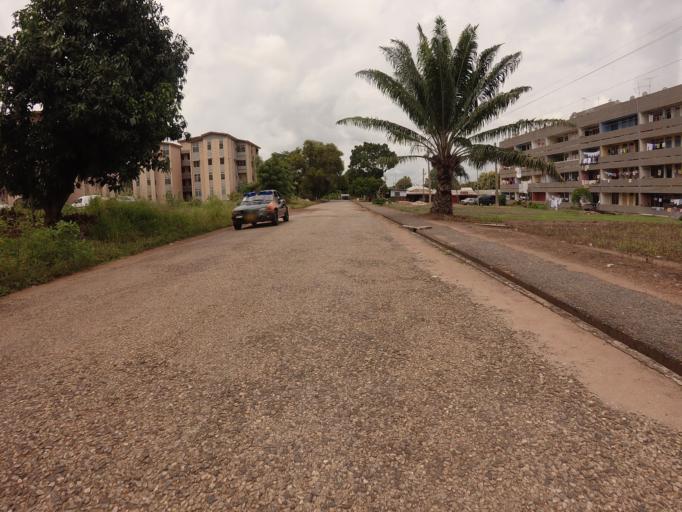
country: GH
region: Volta
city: Ho
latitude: 6.5926
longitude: 0.4613
